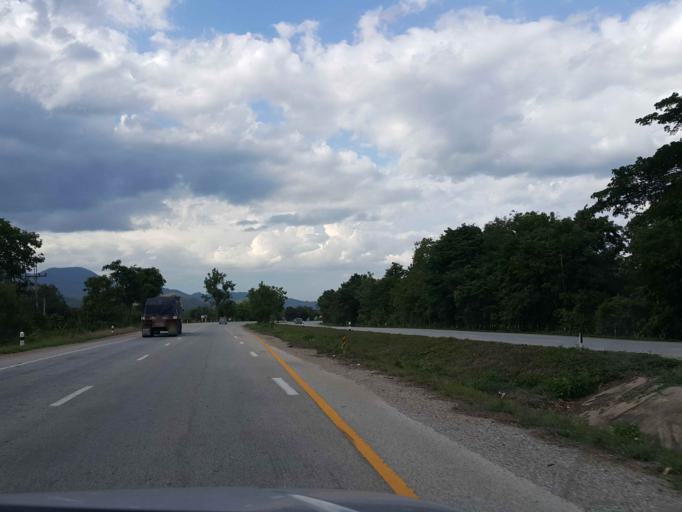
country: TH
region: Lampang
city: Thoen
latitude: 17.7249
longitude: 99.2294
